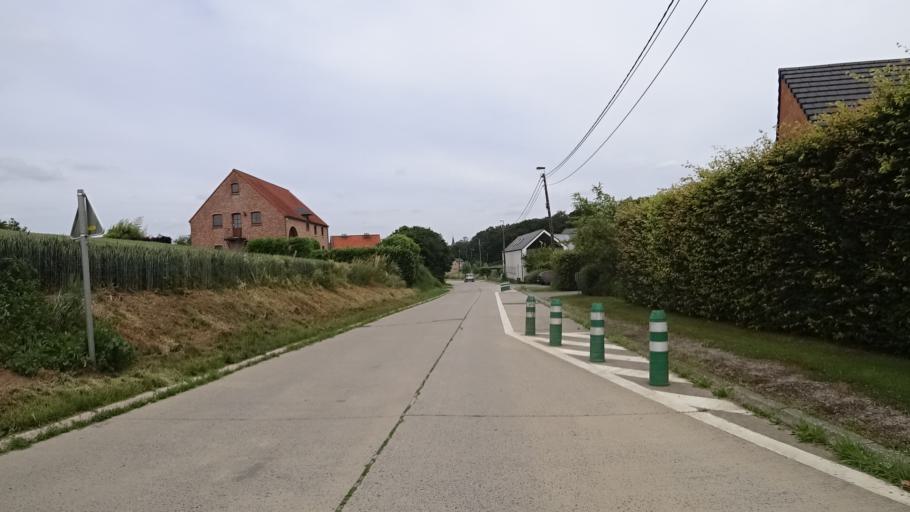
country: BE
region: Wallonia
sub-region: Province du Brabant Wallon
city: Louvain-la-Neuve
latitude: 50.6712
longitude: 4.6504
